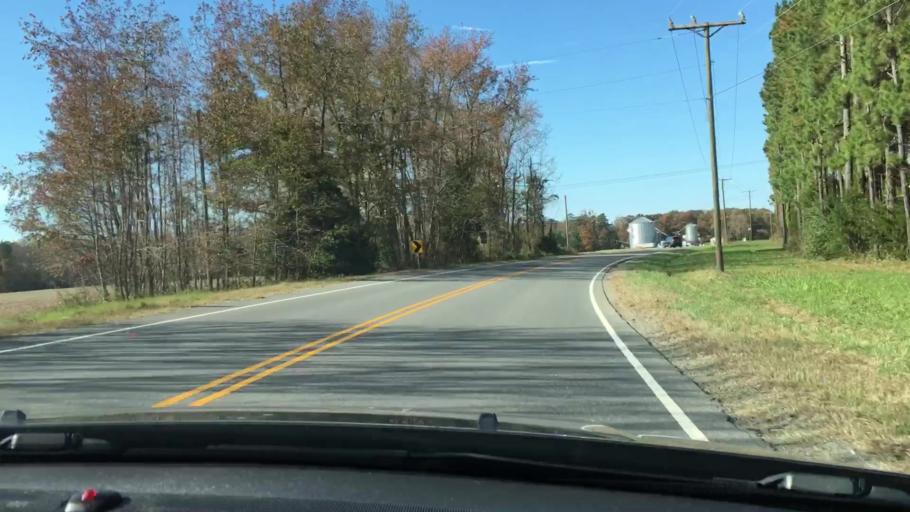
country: US
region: Virginia
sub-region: King and Queen County
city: King and Queen Court House
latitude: 37.5921
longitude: -76.8981
